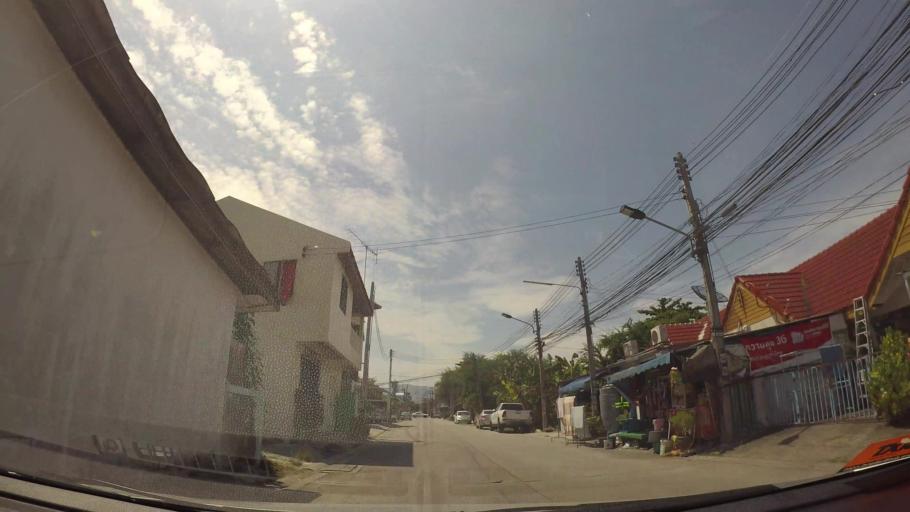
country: TH
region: Chon Buri
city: Chon Buri
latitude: 13.3186
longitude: 100.9553
